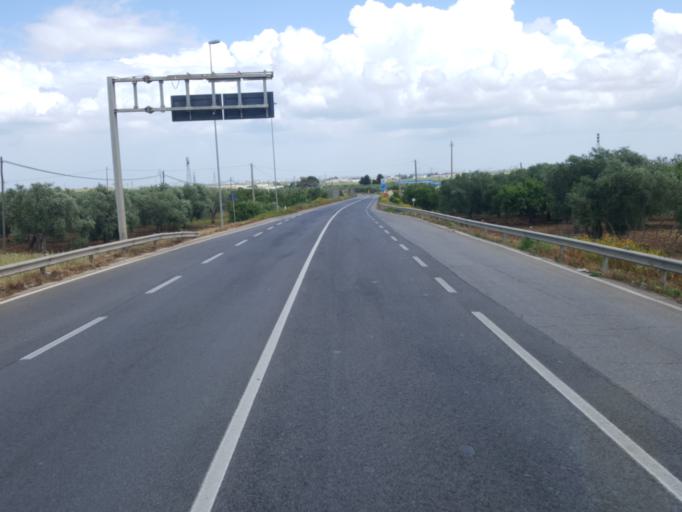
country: IT
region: Apulia
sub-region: Provincia di Bari
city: Palo del Colle
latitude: 41.0566
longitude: 16.7128
